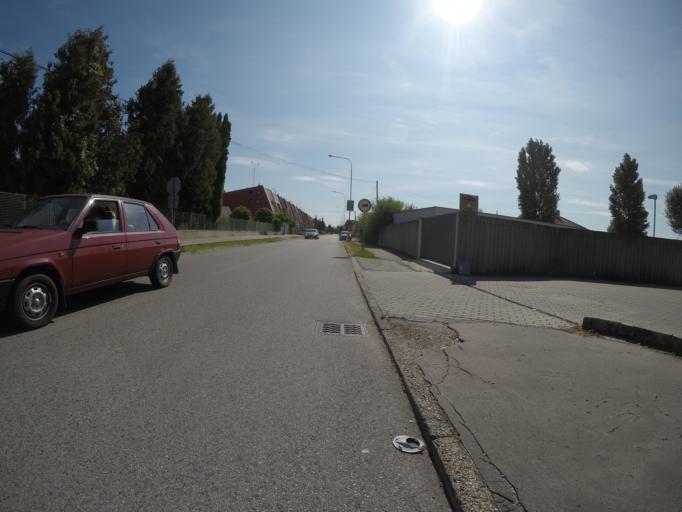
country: SK
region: Trnavsky
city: Dunajska Streda
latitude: 47.9904
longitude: 17.6062
